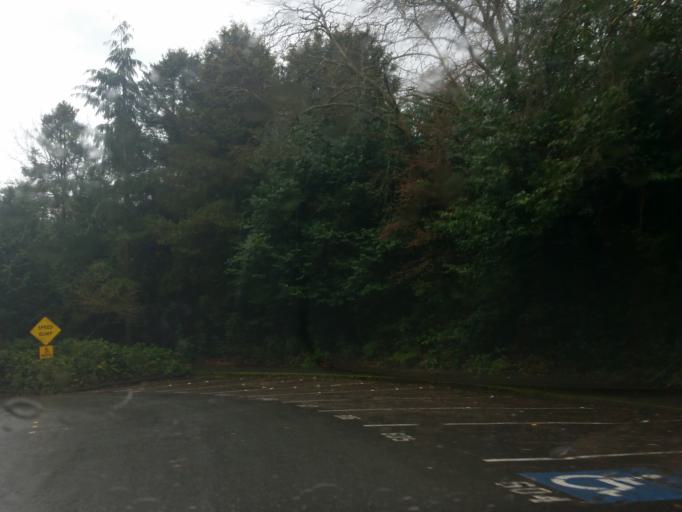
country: US
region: Washington
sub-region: King County
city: Seattle
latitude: 47.6707
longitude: -122.3518
